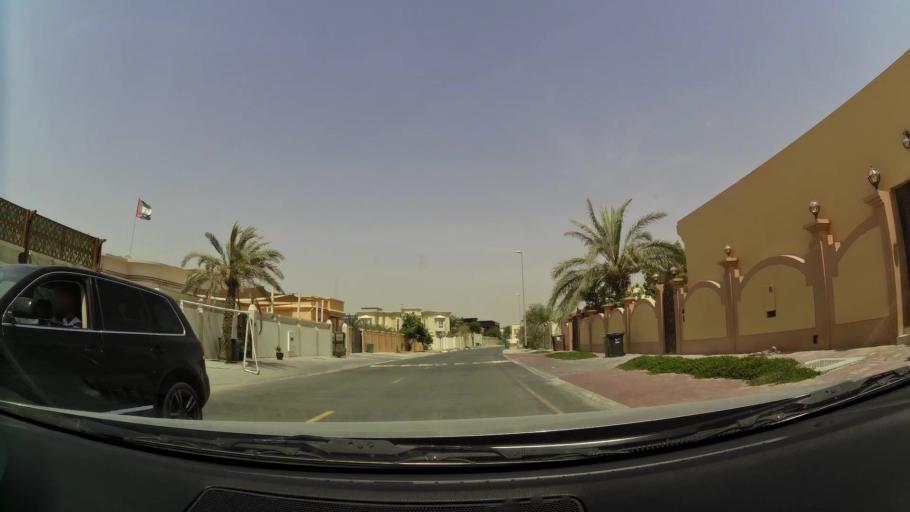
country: AE
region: Ash Shariqah
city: Sharjah
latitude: 25.2442
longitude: 55.4238
